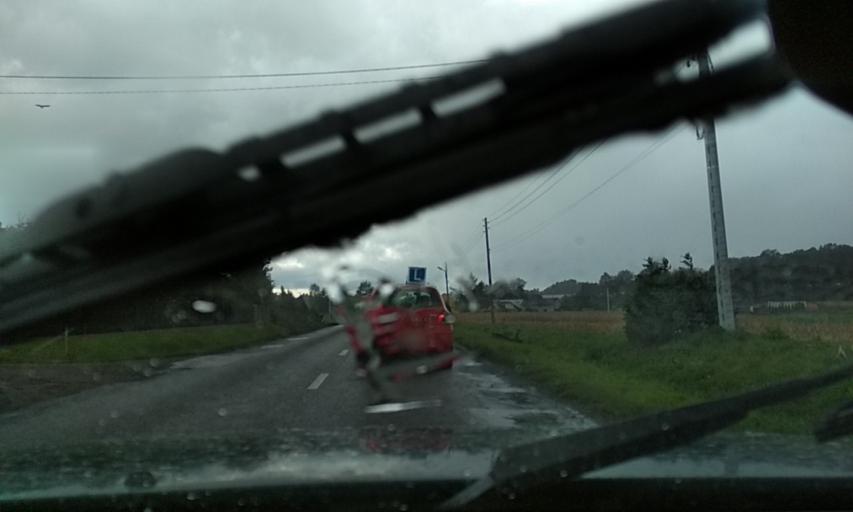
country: PL
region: Silesian Voivodeship
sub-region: Powiat gliwicki
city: Pilchowice
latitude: 50.2142
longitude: 18.5806
